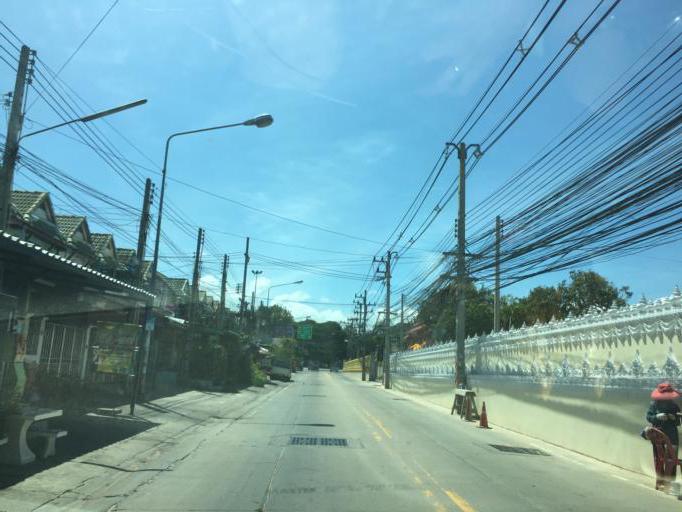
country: TH
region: Chon Buri
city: Phatthaya
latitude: 12.8898
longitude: 100.8960
